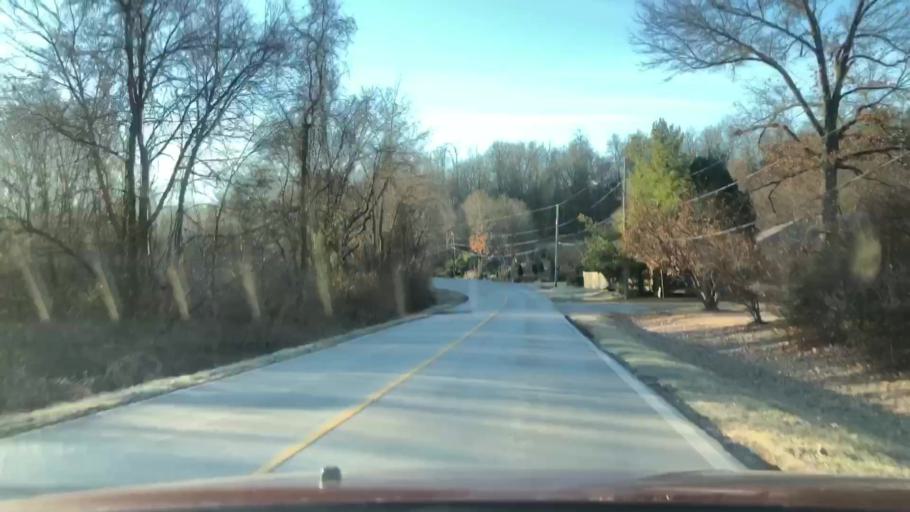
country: US
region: Missouri
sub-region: Greene County
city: Springfield
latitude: 37.1634
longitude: -93.2448
